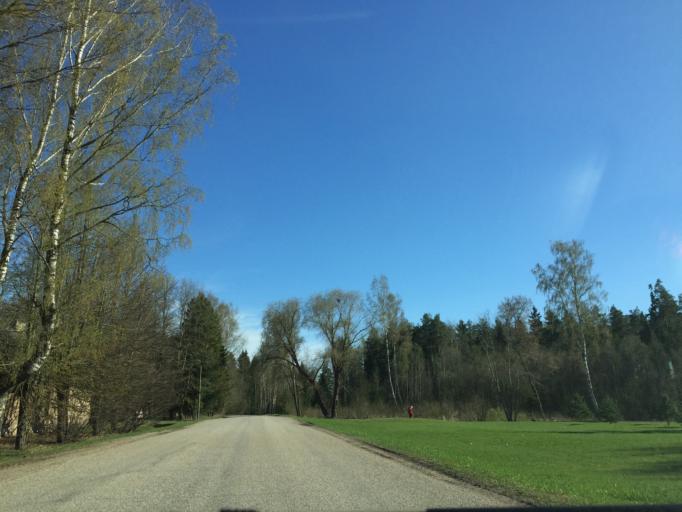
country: EE
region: Valgamaa
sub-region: Valga linn
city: Valga
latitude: 57.8652
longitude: 26.2519
